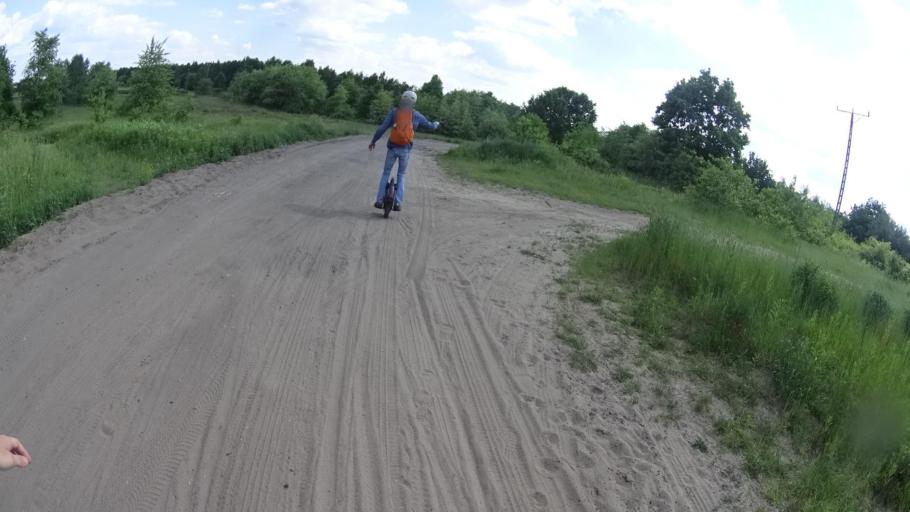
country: PL
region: Masovian Voivodeship
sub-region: Powiat piaseczynski
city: Konstancin-Jeziorna
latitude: 52.0966
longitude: 21.1039
